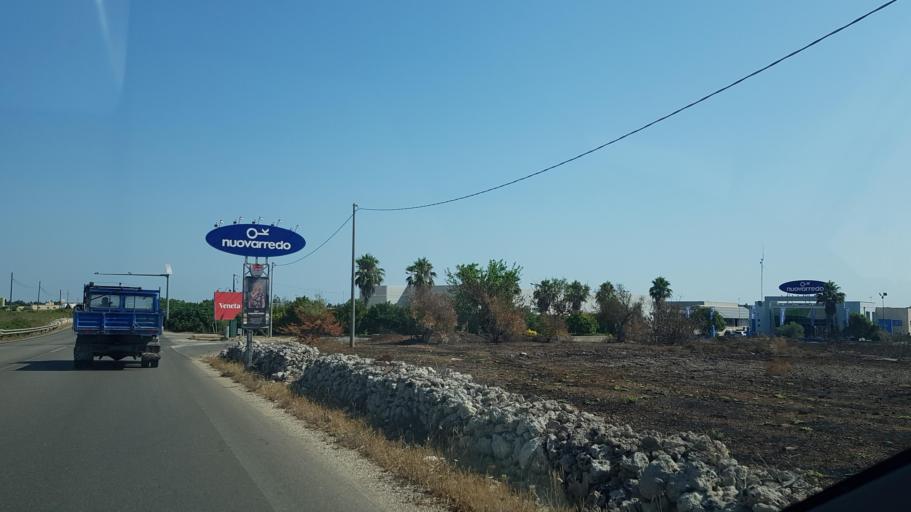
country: IT
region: Apulia
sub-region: Provincia di Lecce
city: Nociglia
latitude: 40.0136
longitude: 18.3242
